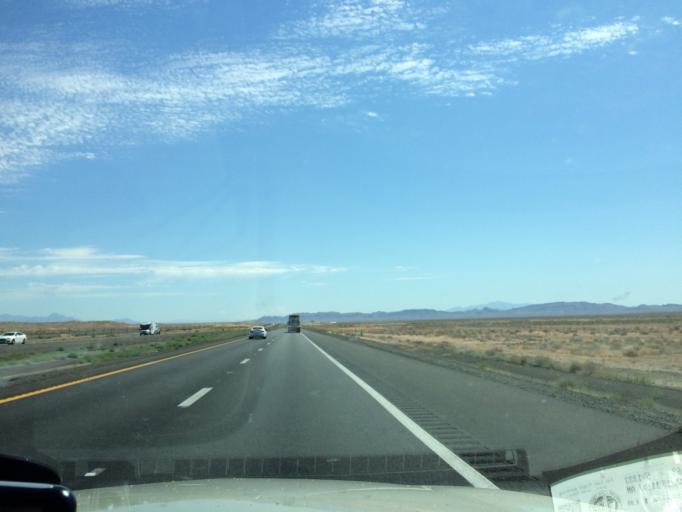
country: US
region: Nevada
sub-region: Clark County
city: Moapa Town
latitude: 36.4803
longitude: -114.8045
